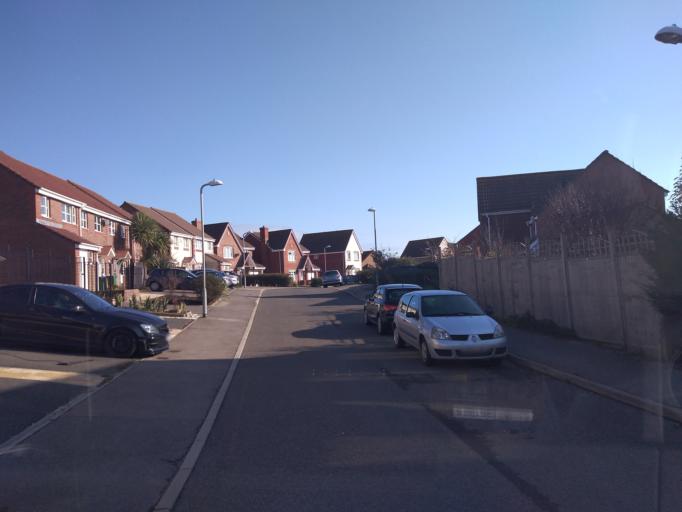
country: GB
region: England
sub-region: East Sussex
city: Newhaven
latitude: 50.7865
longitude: 0.0373
